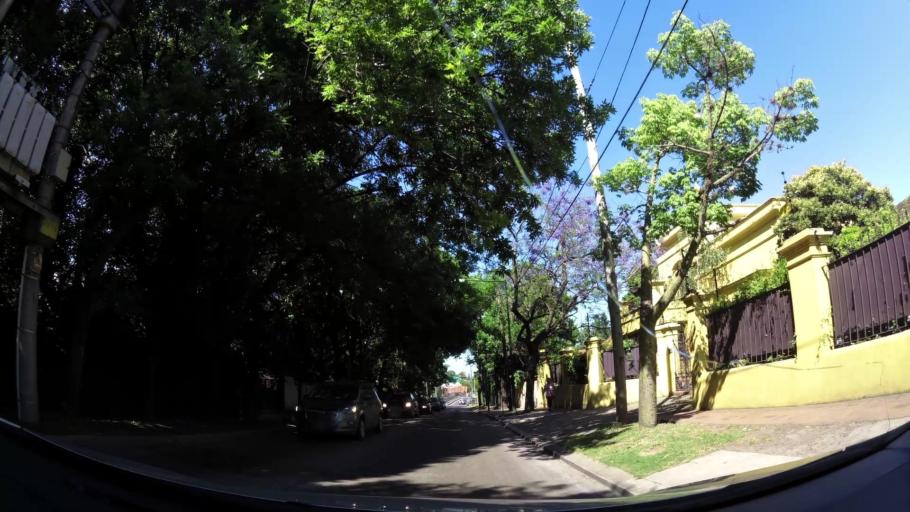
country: AR
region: Buenos Aires
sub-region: Partido de San Isidro
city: San Isidro
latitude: -34.4890
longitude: -58.5675
